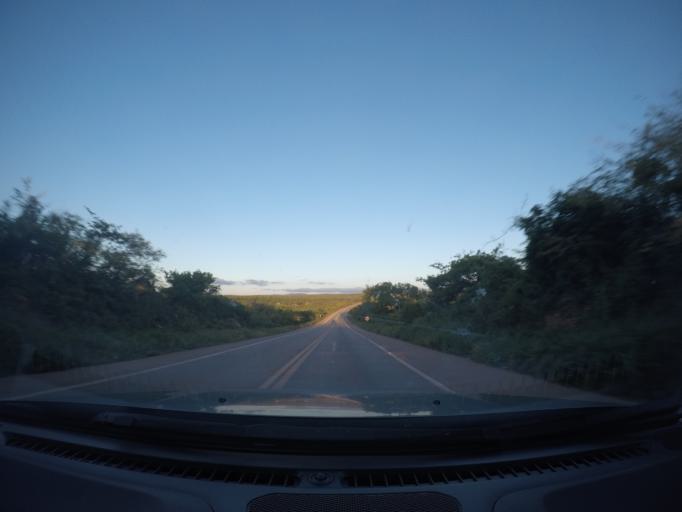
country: BR
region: Bahia
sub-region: Seabra
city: Seabra
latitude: -12.3945
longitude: -41.9286
